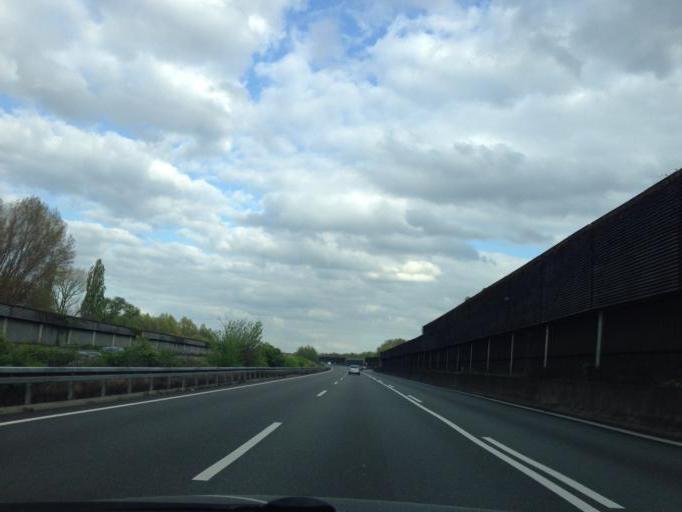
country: DE
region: Lower Saxony
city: Braunschweig
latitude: 52.3138
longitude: 10.5208
